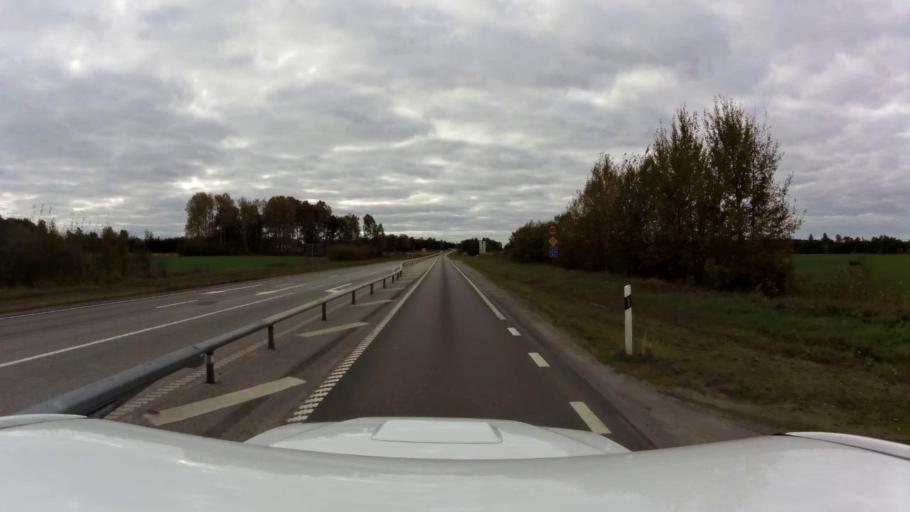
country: SE
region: OEstergoetland
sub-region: Linkopings Kommun
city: Malmslatt
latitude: 58.3709
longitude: 15.5437
